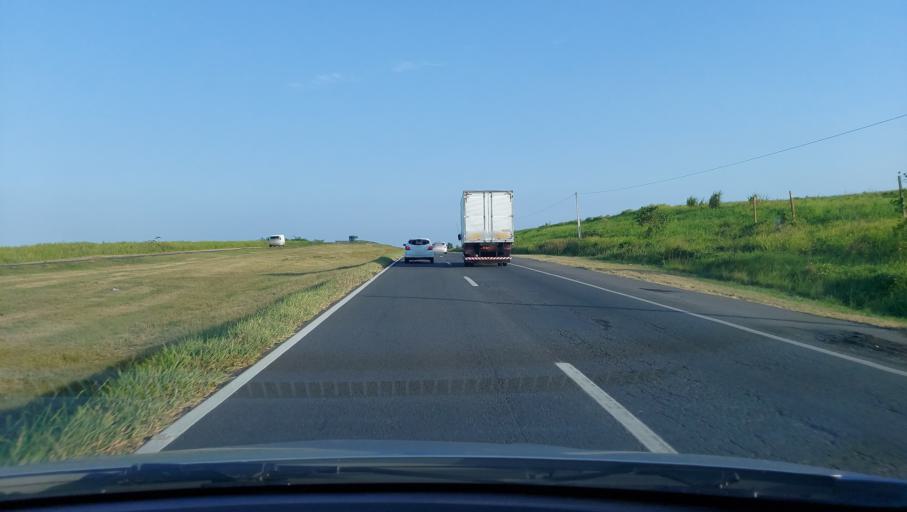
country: BR
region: Bahia
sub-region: Santo Amaro
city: Santo Amaro
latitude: -12.5057
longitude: -38.6358
